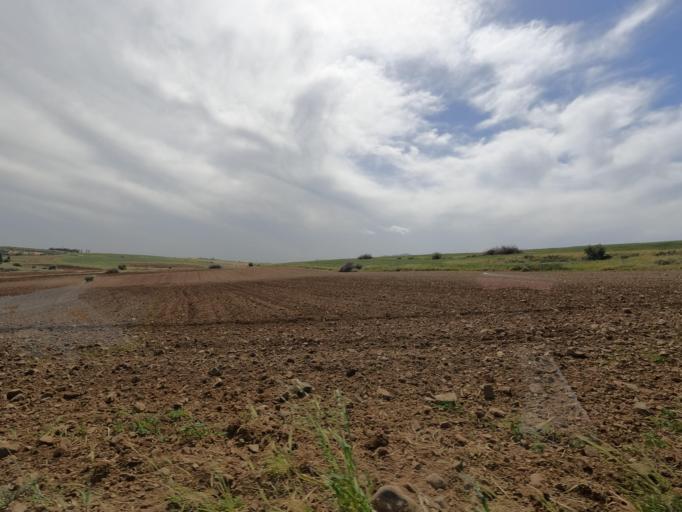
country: CY
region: Lefkosia
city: Astromeritis
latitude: 35.1047
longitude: 32.9580
